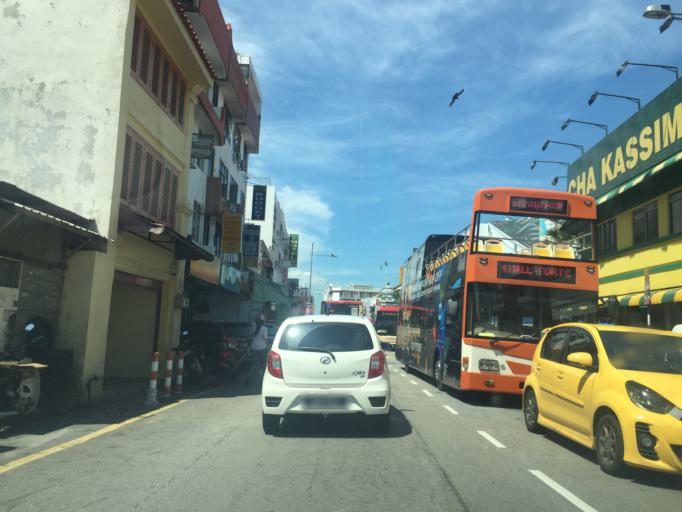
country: MY
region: Penang
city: George Town
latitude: 5.4155
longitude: 100.3394
